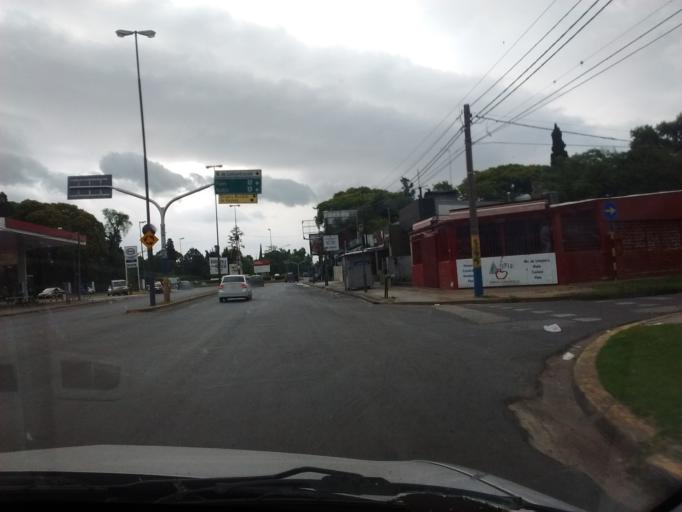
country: AR
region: Santa Fe
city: Funes
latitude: -32.9285
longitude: -60.7378
